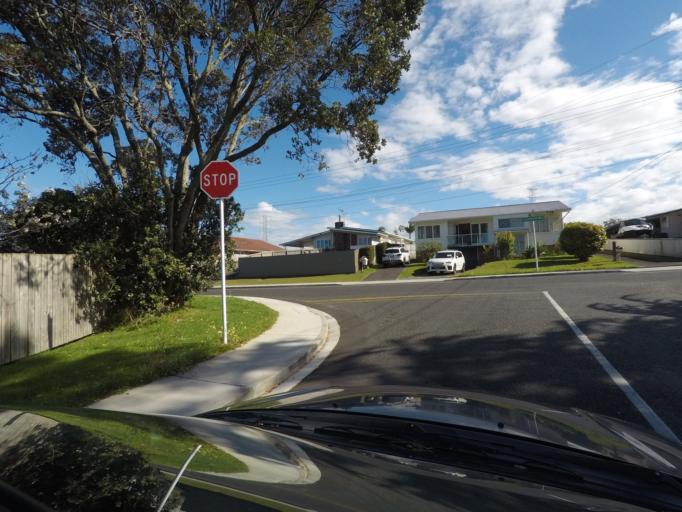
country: NZ
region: Auckland
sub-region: Auckland
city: Rosebank
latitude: -36.8659
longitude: 174.6501
